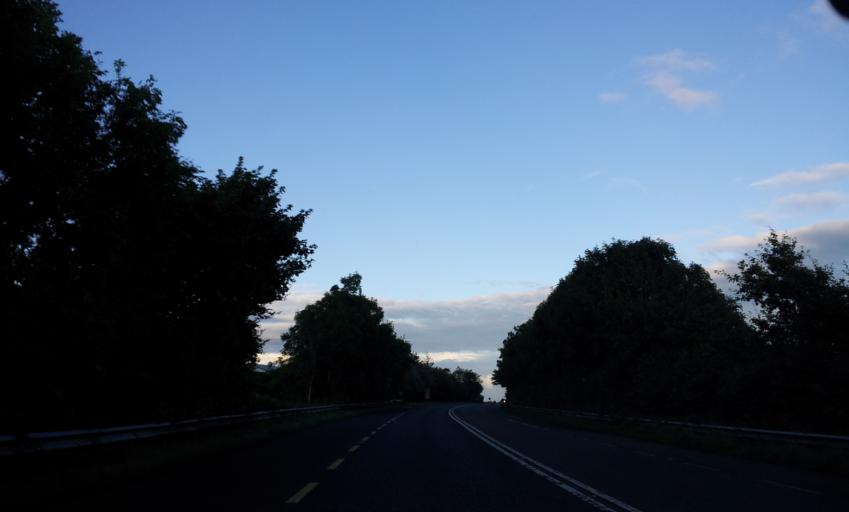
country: IE
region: Munster
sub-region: County Limerick
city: Newcastle West
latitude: 52.4196
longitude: -9.1424
